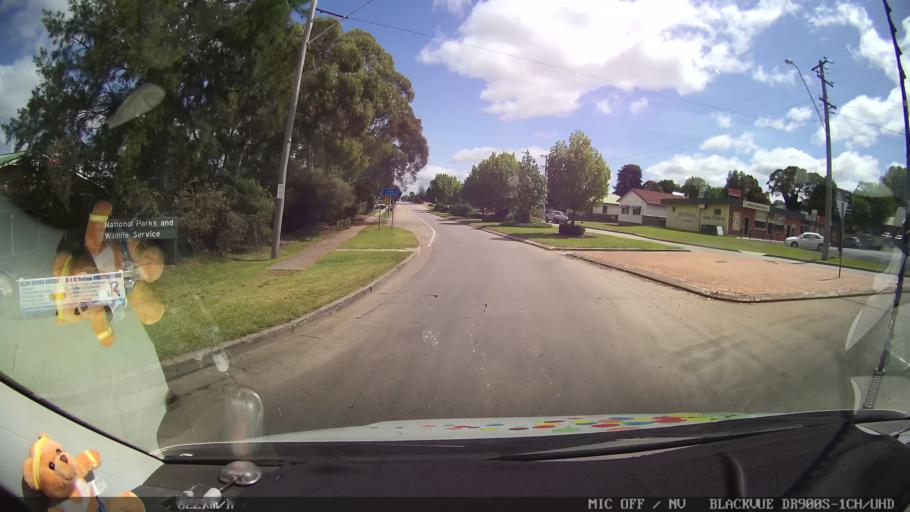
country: AU
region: New South Wales
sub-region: Glen Innes Severn
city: Glen Innes
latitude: -29.7474
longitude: 151.7363
